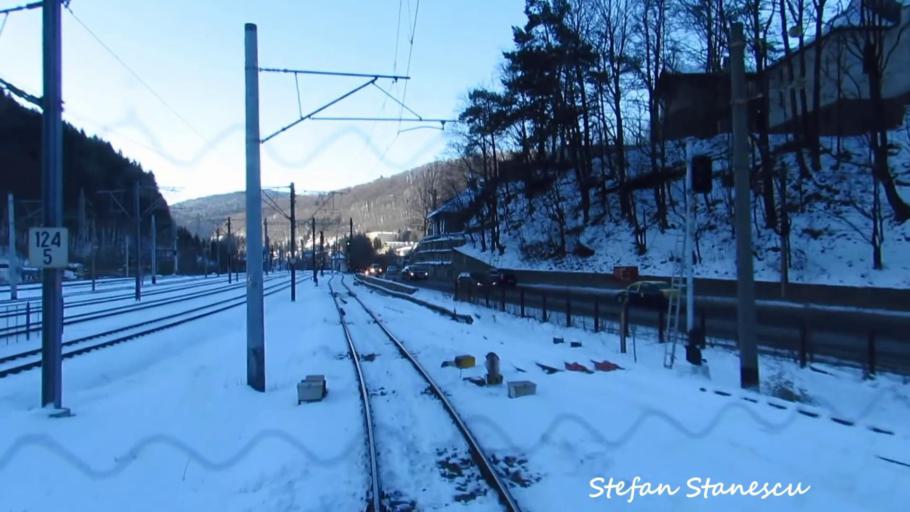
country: RO
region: Prahova
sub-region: Oras Sinaia
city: Sinaia
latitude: 45.3526
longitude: 25.5533
